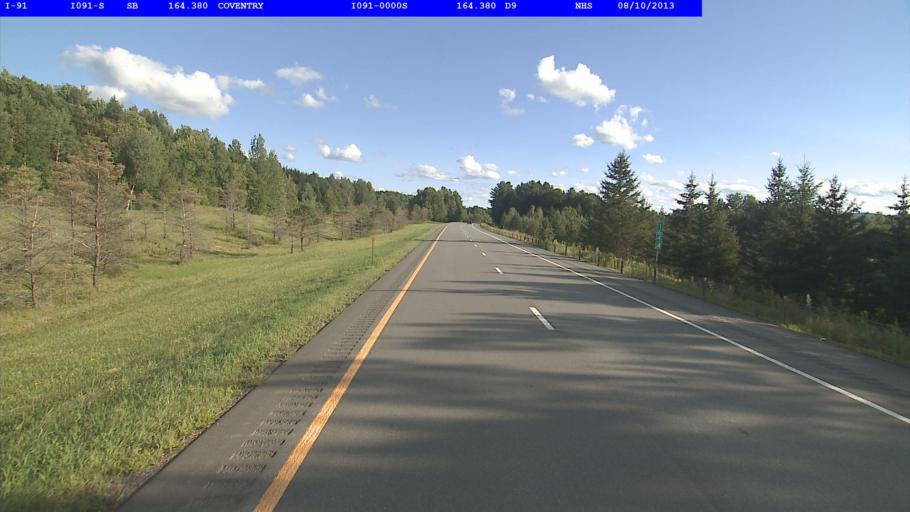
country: US
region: Vermont
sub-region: Orleans County
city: Newport
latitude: 44.8461
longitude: -72.1936
